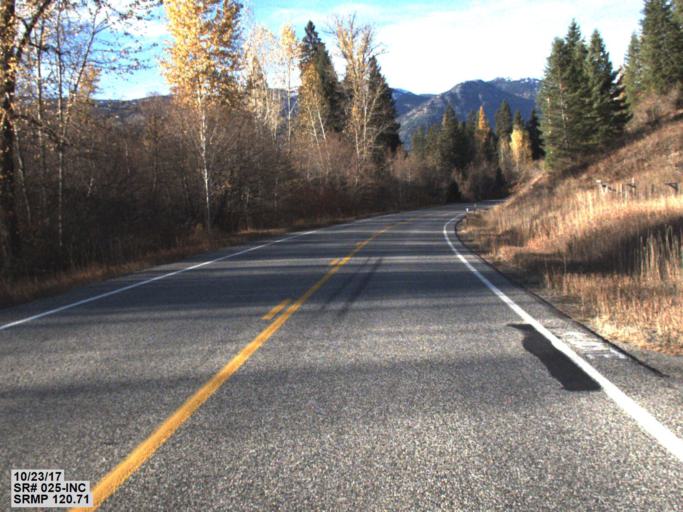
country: CA
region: British Columbia
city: Rossland
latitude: 48.9932
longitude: -117.8307
